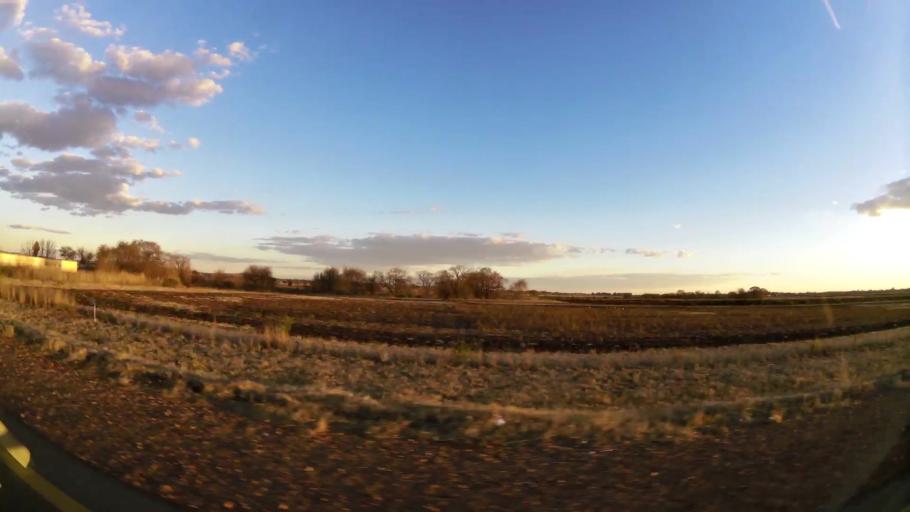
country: ZA
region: North-West
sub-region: Dr Kenneth Kaunda District Municipality
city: Potchefstroom
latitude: -26.7287
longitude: 27.1236
